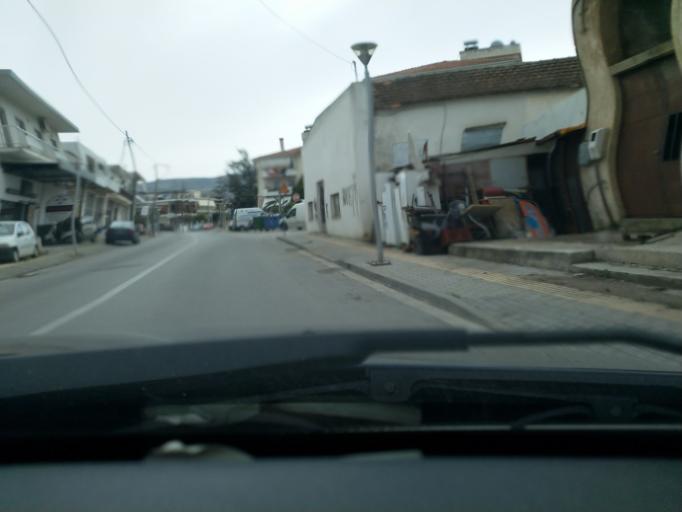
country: GR
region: Crete
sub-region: Nomos Chanias
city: Chania
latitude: 35.4965
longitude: 24.0219
